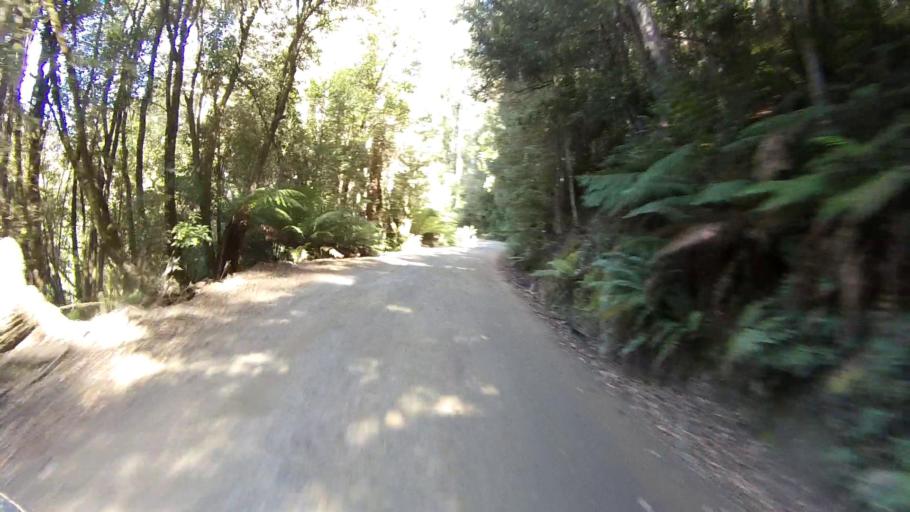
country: AU
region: Tasmania
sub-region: Derwent Valley
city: New Norfolk
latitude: -42.6761
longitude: 146.6941
